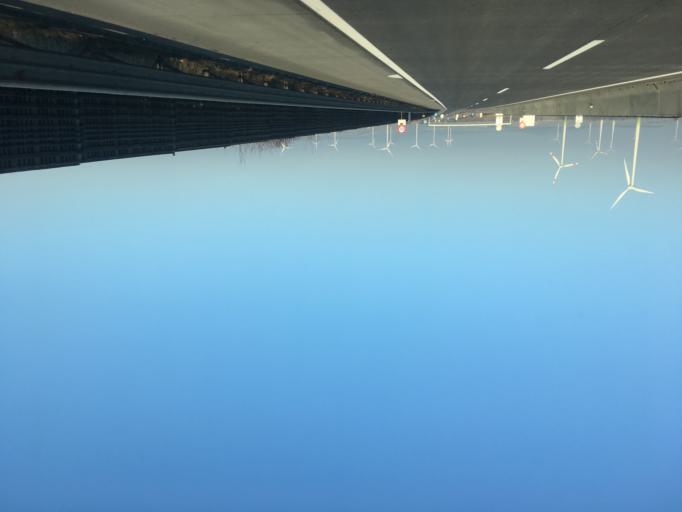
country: AT
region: Burgenland
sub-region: Politischer Bezirk Neusiedl am See
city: Kittsee
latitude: 48.0744
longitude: 17.0616
